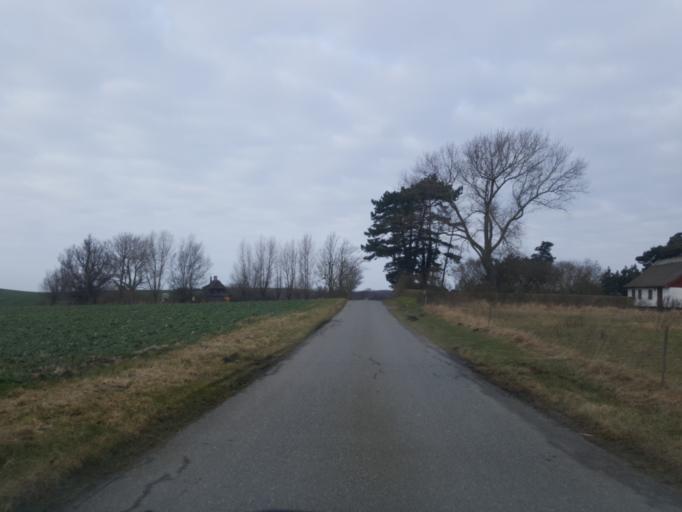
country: DK
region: Zealand
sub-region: Vordingborg Kommune
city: Neder Vindinge
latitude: 55.0509
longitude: 11.7691
